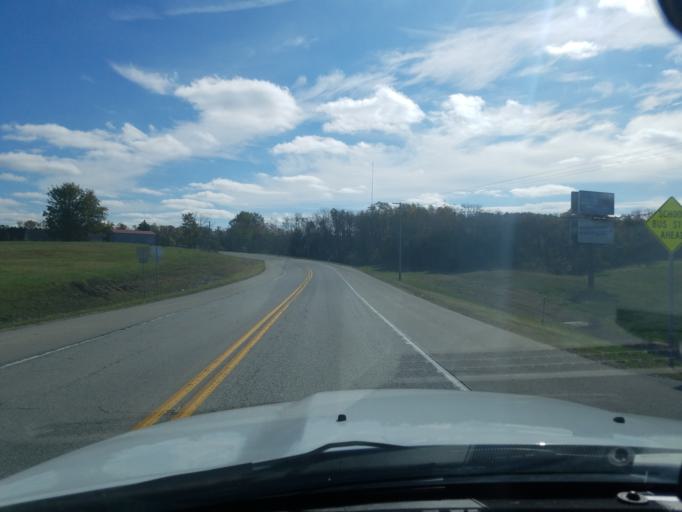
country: US
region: Indiana
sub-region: Ripley County
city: Versailles
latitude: 39.0726
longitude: -85.2701
